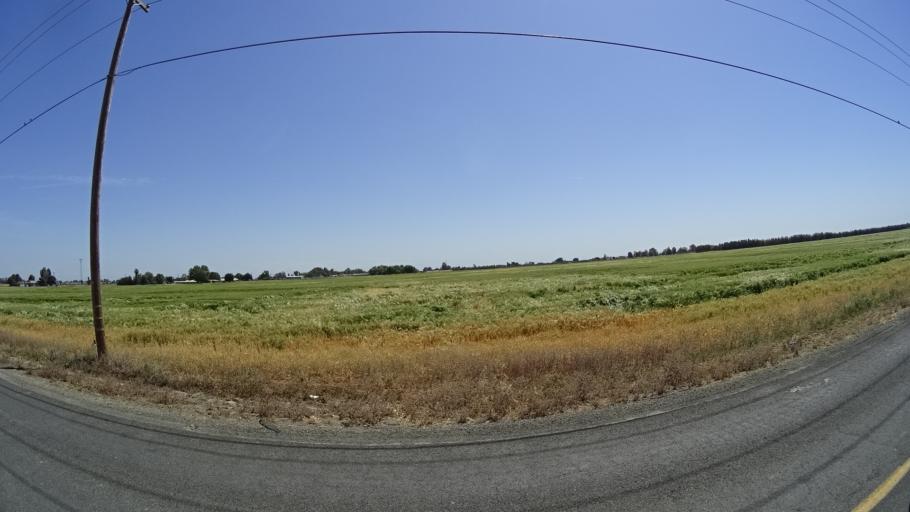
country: US
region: California
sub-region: Kings County
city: Lemoore
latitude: 36.2667
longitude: -119.7991
